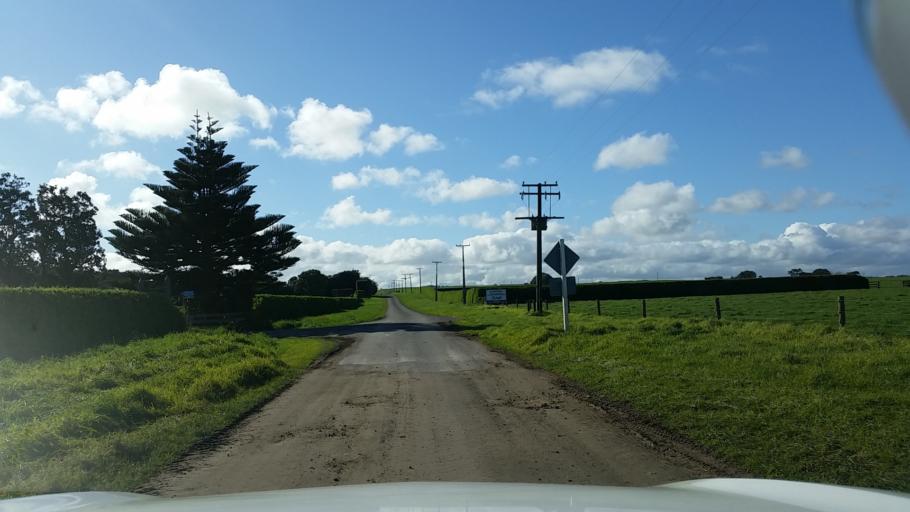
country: NZ
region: Taranaki
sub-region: South Taranaki District
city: Patea
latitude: -39.6843
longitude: 174.4004
